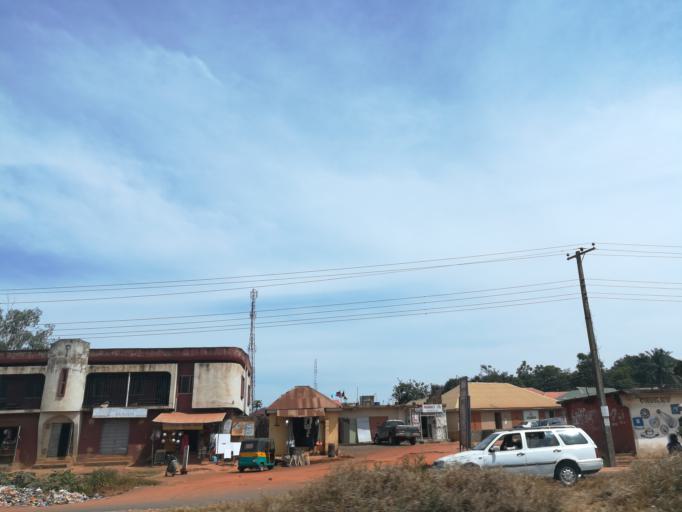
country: NG
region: Plateau
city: Bukuru
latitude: 9.7908
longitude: 8.8592
